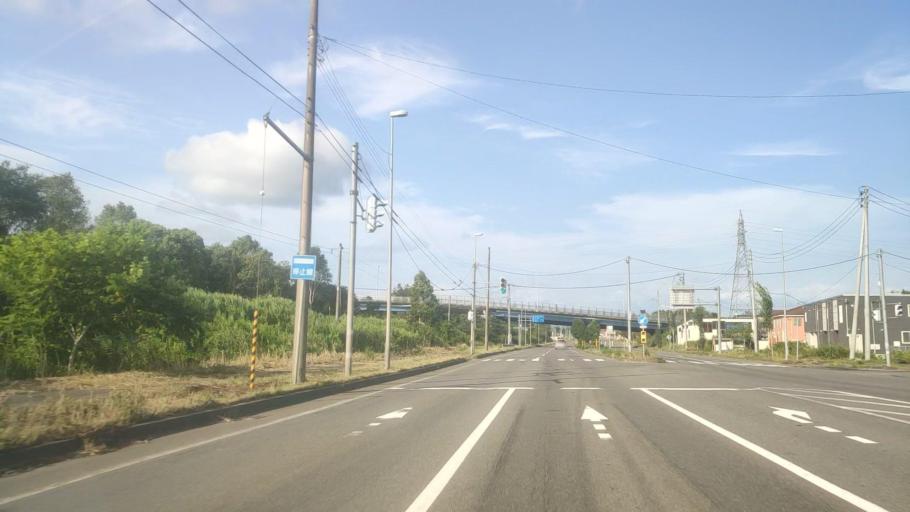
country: JP
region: Hokkaido
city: Chitose
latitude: 42.7609
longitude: 141.8089
